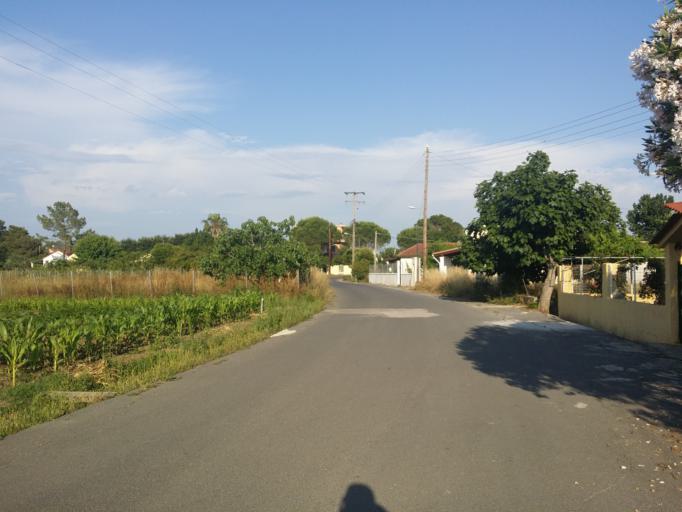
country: GR
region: Ionian Islands
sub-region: Nomos Kerkyras
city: Perivoli
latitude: 39.4286
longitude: 19.9464
